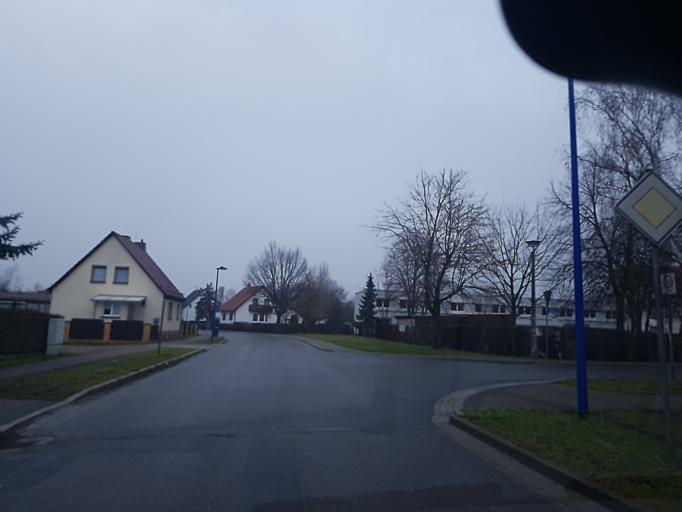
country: DE
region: Brandenburg
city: Finsterwalde
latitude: 51.6220
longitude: 13.7063
